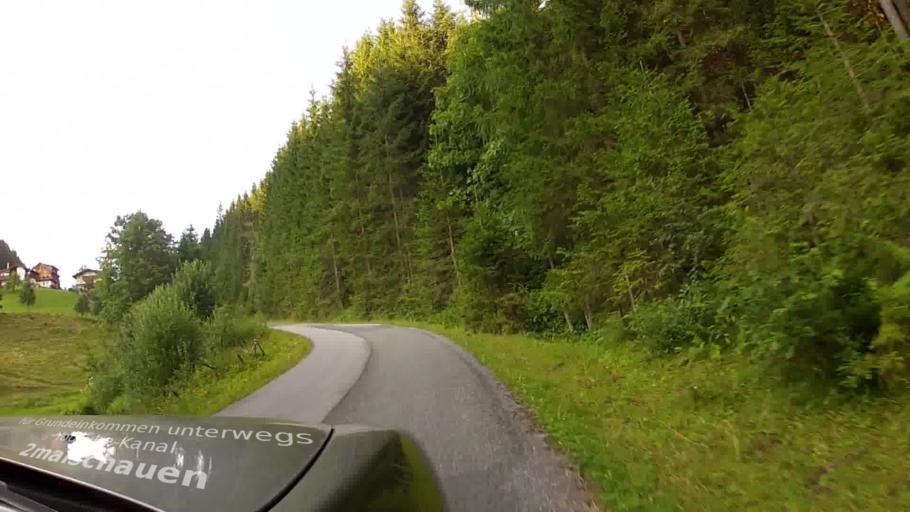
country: AT
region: Salzburg
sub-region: Politischer Bezirk Sankt Johann im Pongau
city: Eben im Pongau
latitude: 47.4364
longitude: 13.3822
